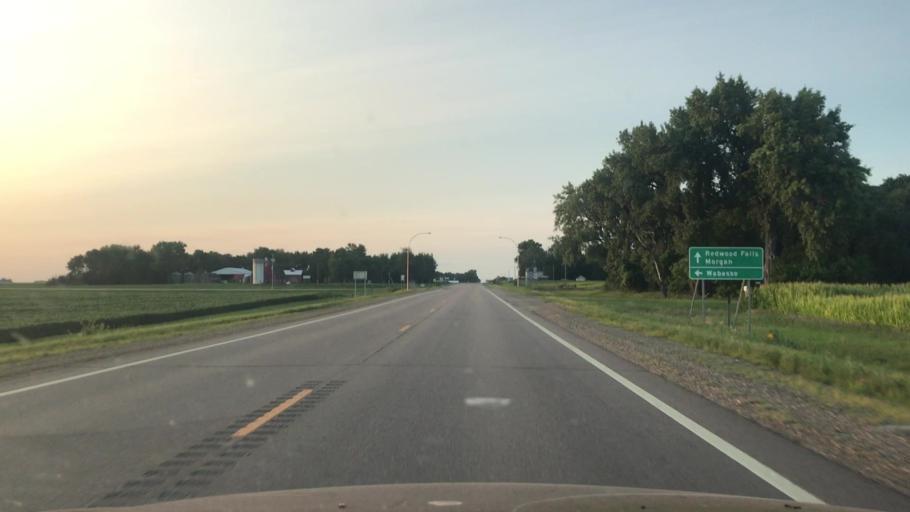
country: US
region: Minnesota
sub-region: Redwood County
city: Redwood Falls
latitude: 44.4039
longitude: -95.1275
